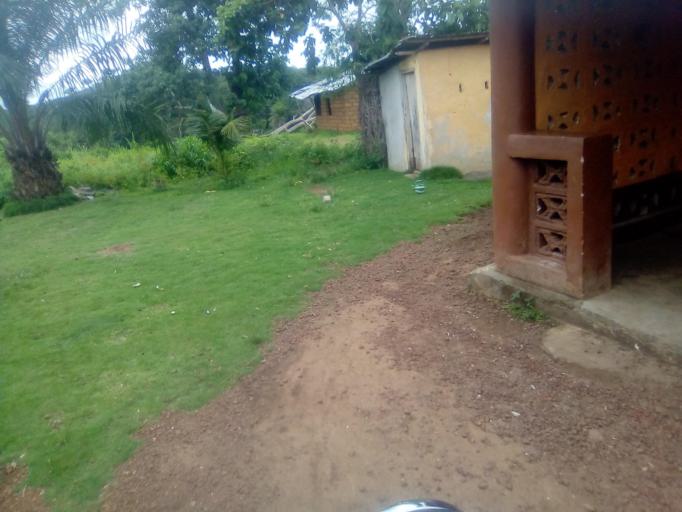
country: SL
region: Southern Province
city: Moyamba
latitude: 8.1457
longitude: -12.4337
